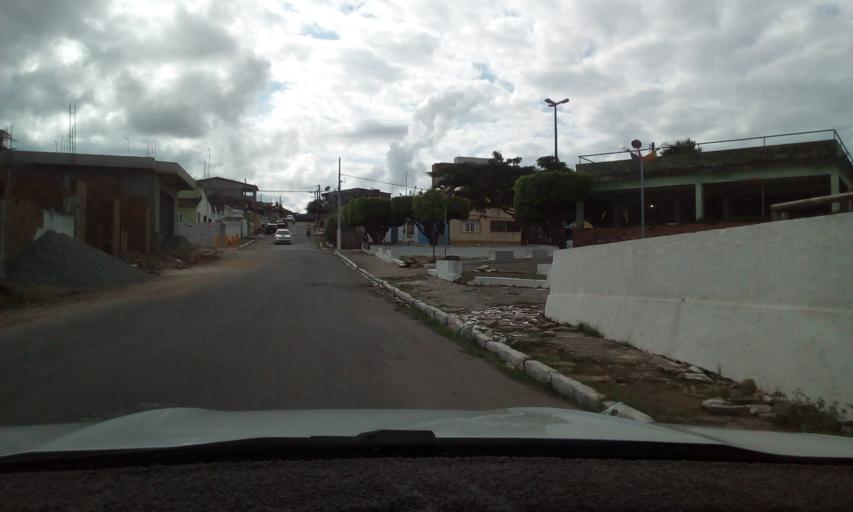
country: BR
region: Paraiba
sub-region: Mamanguape
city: Mamanguape
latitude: -6.8338
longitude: -35.1194
